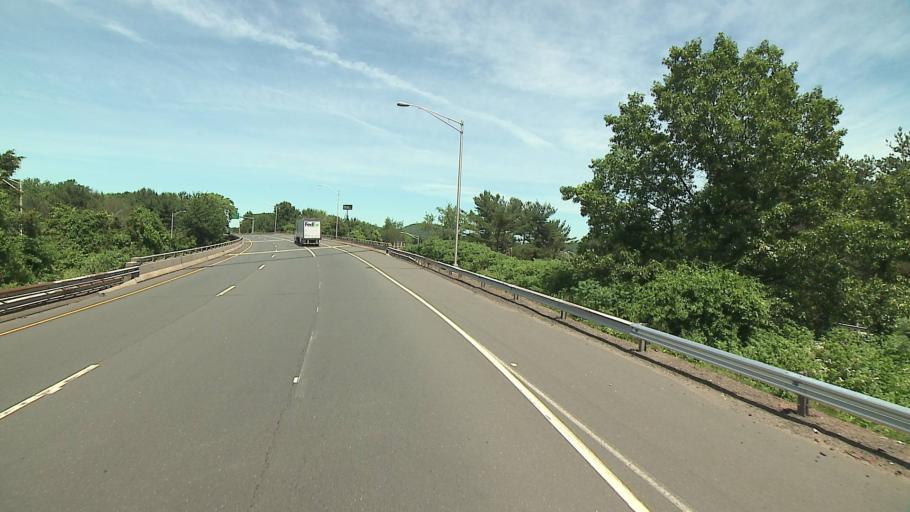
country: US
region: Connecticut
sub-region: New Haven County
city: Meriden
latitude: 41.5328
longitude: -72.7677
